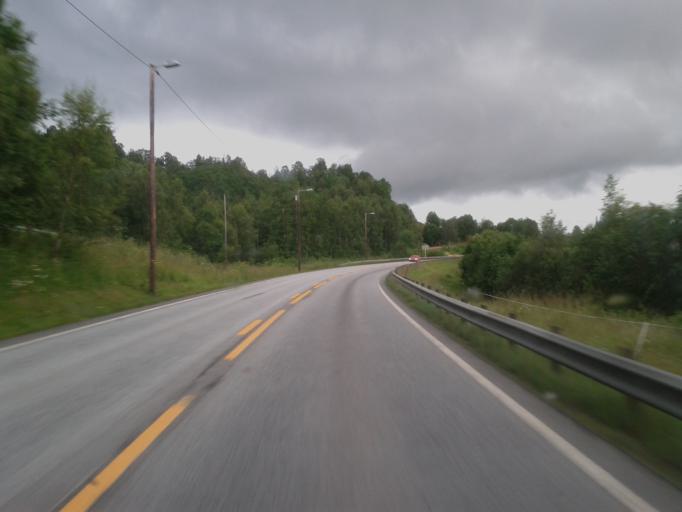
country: NO
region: Sor-Trondelag
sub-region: Melhus
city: Lundamo
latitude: 63.1145
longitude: 10.2415
